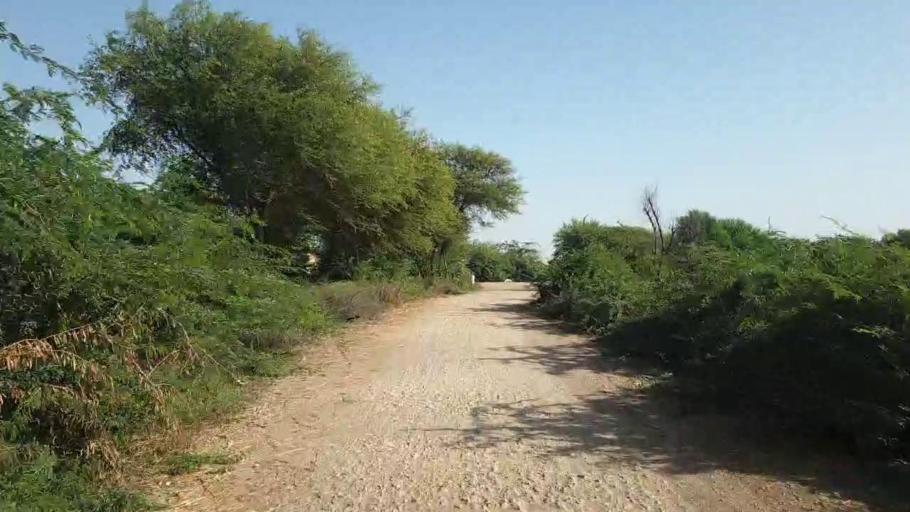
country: PK
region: Sindh
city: Badin
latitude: 24.6014
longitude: 68.9149
